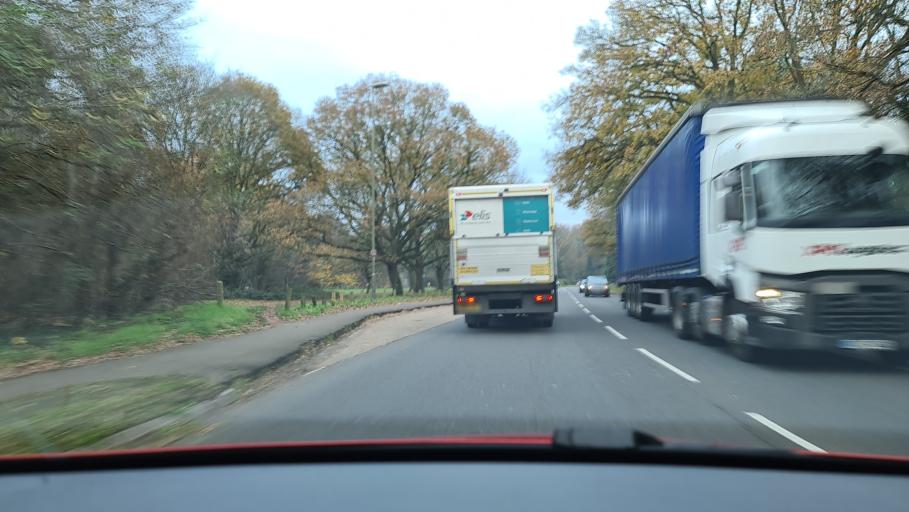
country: GB
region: England
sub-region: Surrey
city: Hinchley Wood
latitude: 51.3799
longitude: -0.3479
